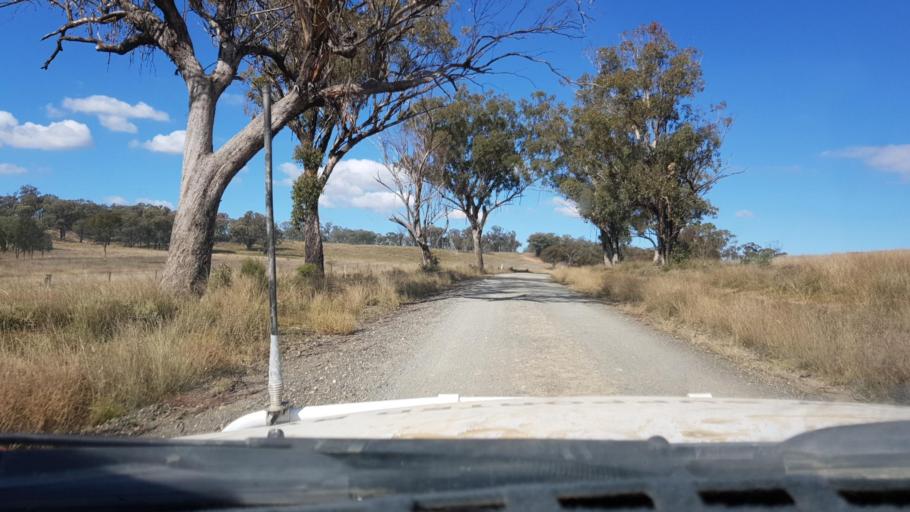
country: AU
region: New South Wales
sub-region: Tamworth Municipality
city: Manilla
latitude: -30.4599
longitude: 150.7429
